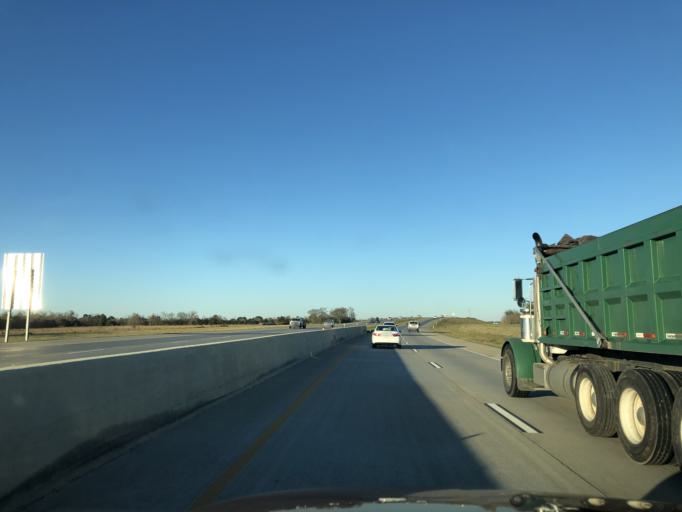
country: US
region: Texas
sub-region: Harris County
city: Cypress
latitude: 30.0318
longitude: -95.7642
